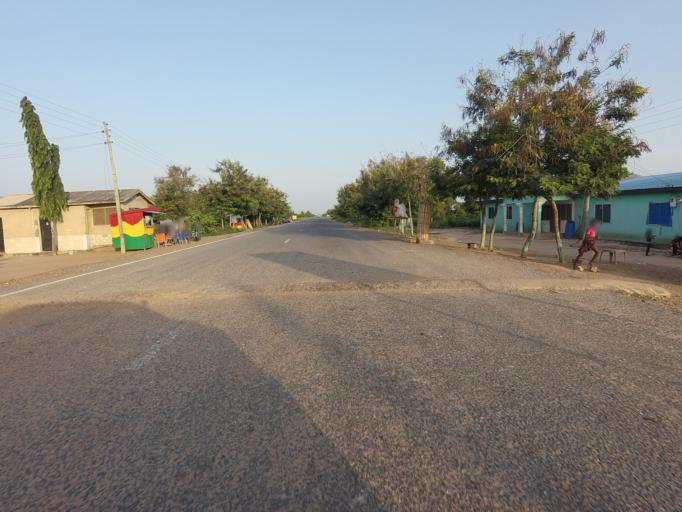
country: GH
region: Volta
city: Anloga
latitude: 5.8923
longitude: 0.7178
